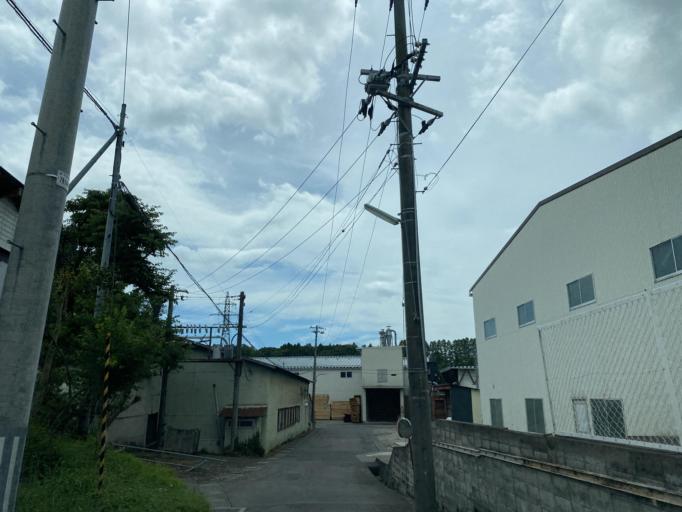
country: JP
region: Fukushima
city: Koriyama
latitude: 37.3614
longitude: 140.3470
